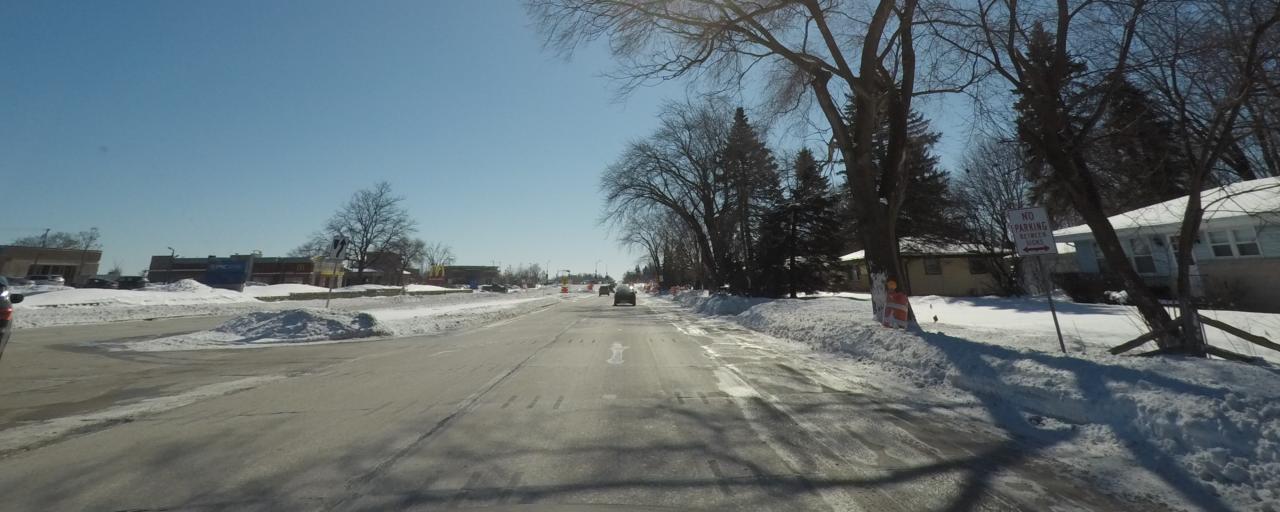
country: US
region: Wisconsin
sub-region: Waukesha County
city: New Berlin
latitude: 42.9790
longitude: -88.1085
